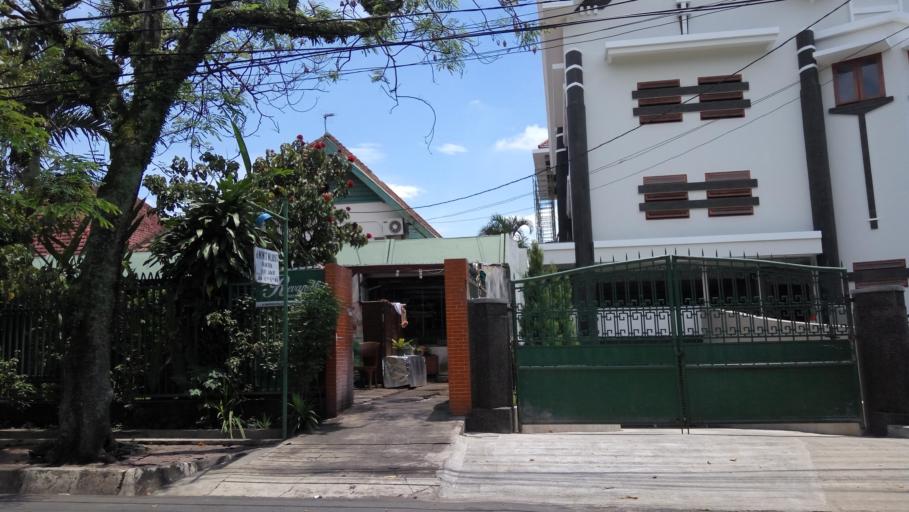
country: ID
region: East Java
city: Malang
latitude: -7.9788
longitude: 112.6252
